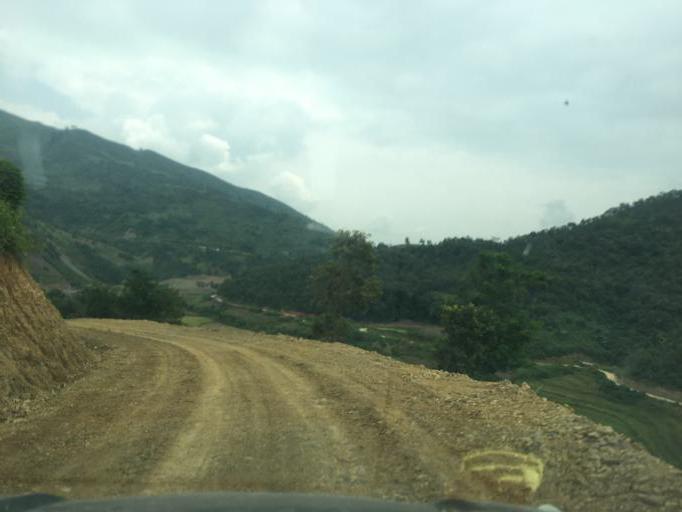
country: CN
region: Guangxi Zhuangzu Zizhiqu
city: Tongle
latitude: 25.1222
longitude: 106.4132
